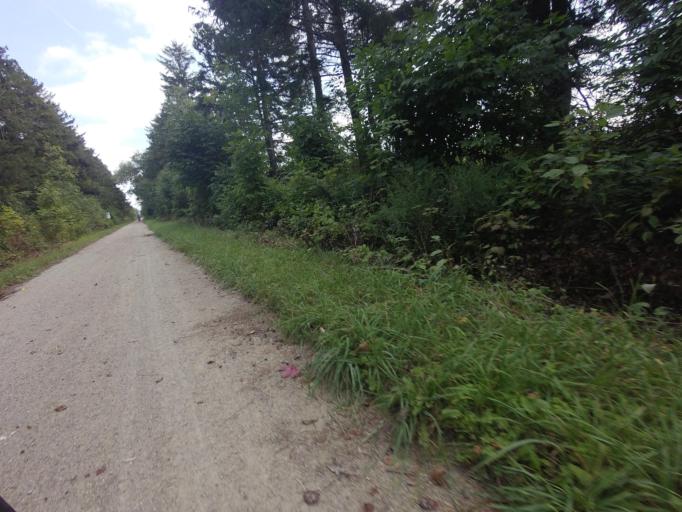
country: CA
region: Ontario
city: North Perth
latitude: 43.5781
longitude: -80.7867
